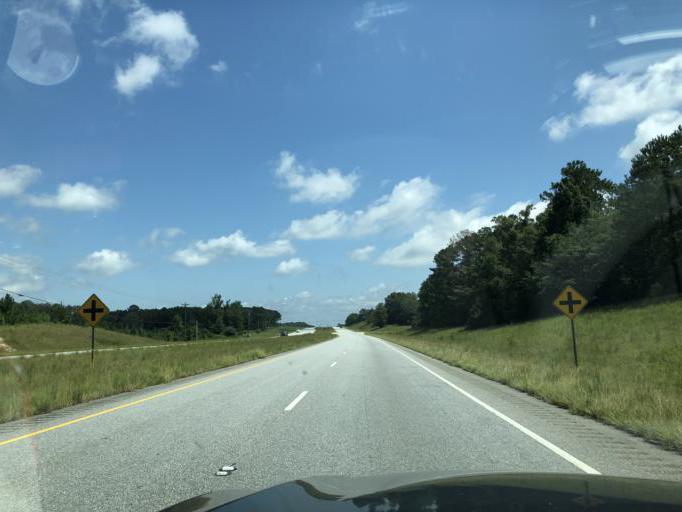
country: US
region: Alabama
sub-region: Barbour County
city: Eufaula
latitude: 31.7566
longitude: -85.2129
